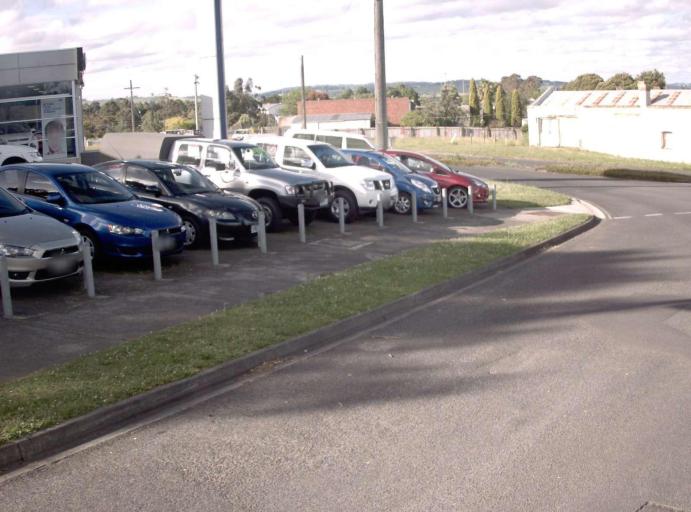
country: AU
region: Victoria
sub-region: Baw Baw
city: Warragul
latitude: -38.4756
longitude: 145.9474
